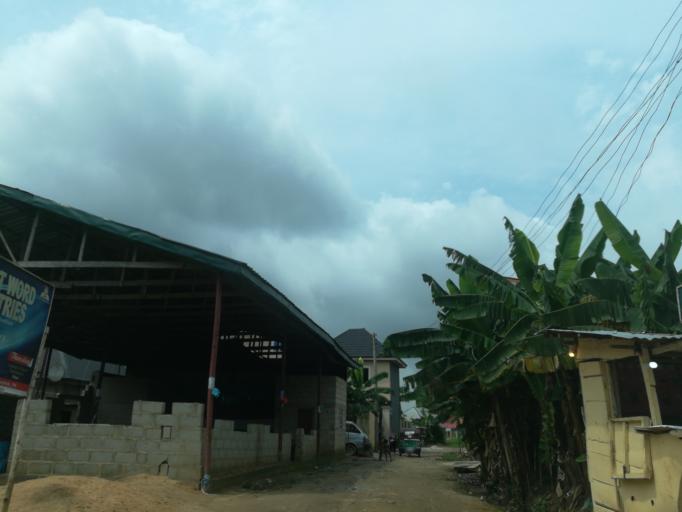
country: NG
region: Rivers
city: Port Harcourt
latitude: 4.8918
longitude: 6.9829
